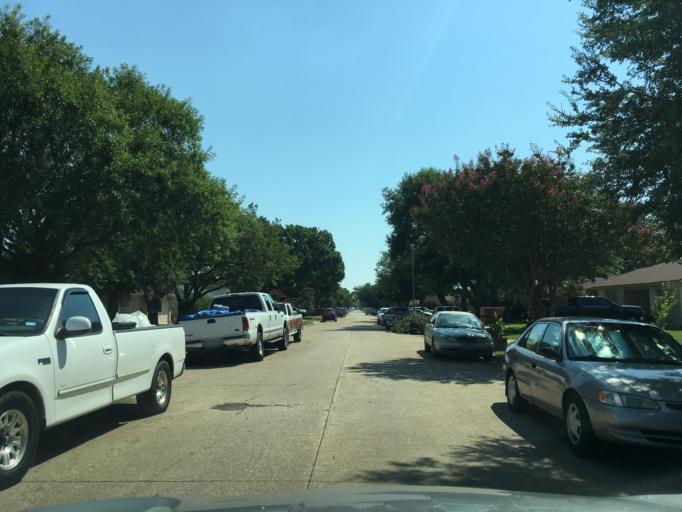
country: US
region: Texas
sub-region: Dallas County
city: Garland
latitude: 32.9382
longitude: -96.6555
